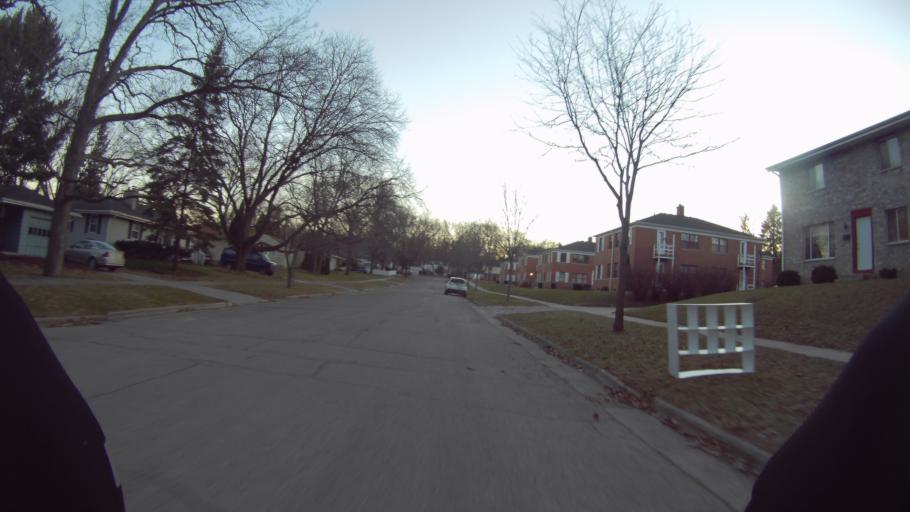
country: US
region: Wisconsin
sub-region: Dane County
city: Shorewood Hills
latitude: 43.0620
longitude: -89.4529
